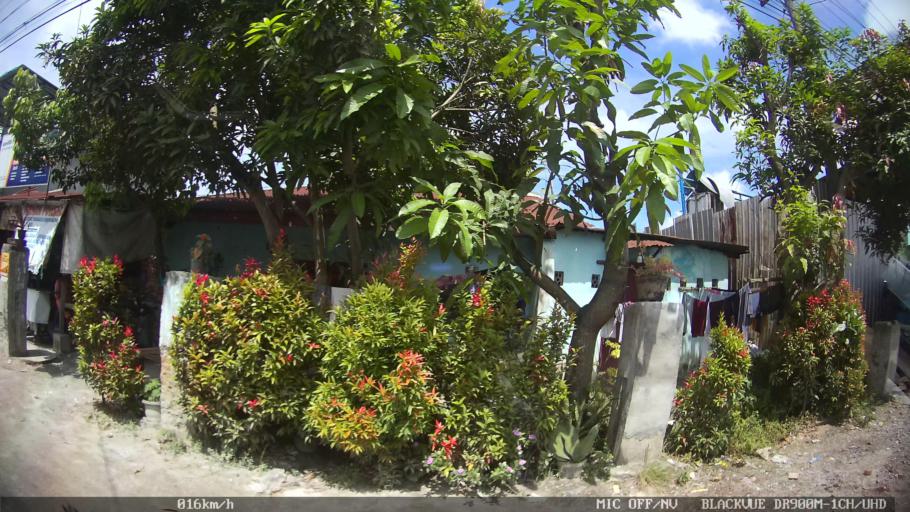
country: ID
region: North Sumatra
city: Percut
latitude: 3.6028
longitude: 98.7875
